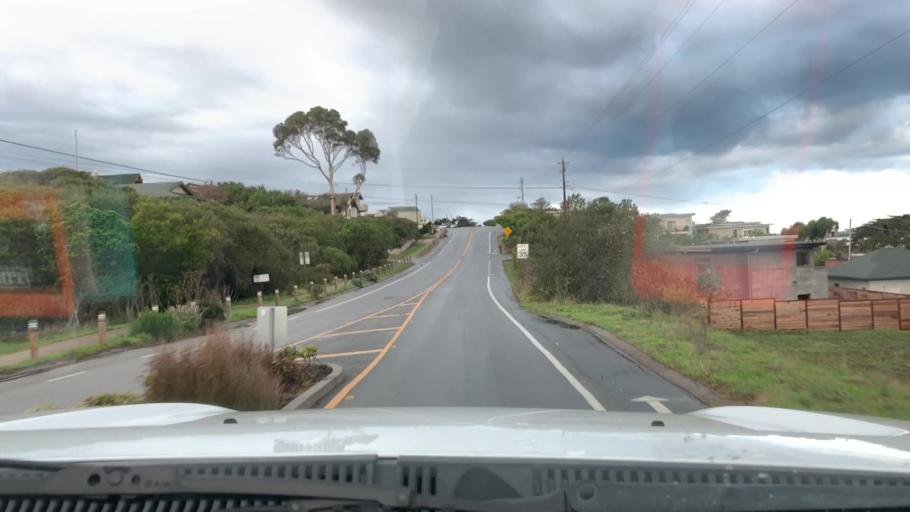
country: US
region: California
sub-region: San Luis Obispo County
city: Los Osos
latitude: 35.3300
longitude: -120.8333
